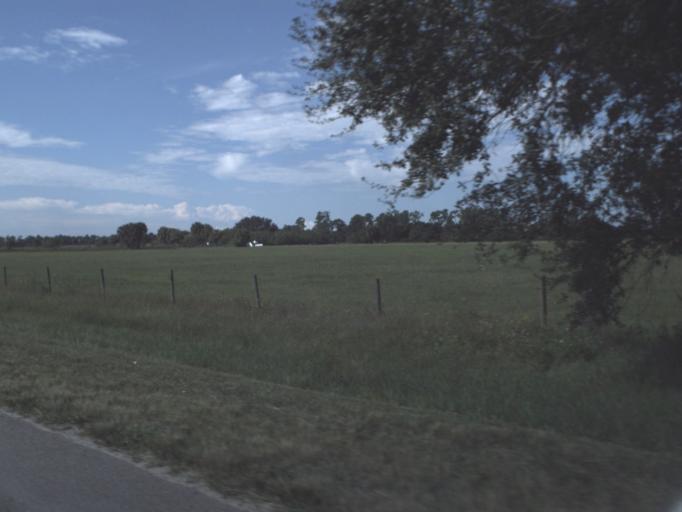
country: US
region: Florida
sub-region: Collier County
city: Immokalee
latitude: 26.5292
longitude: -81.4353
